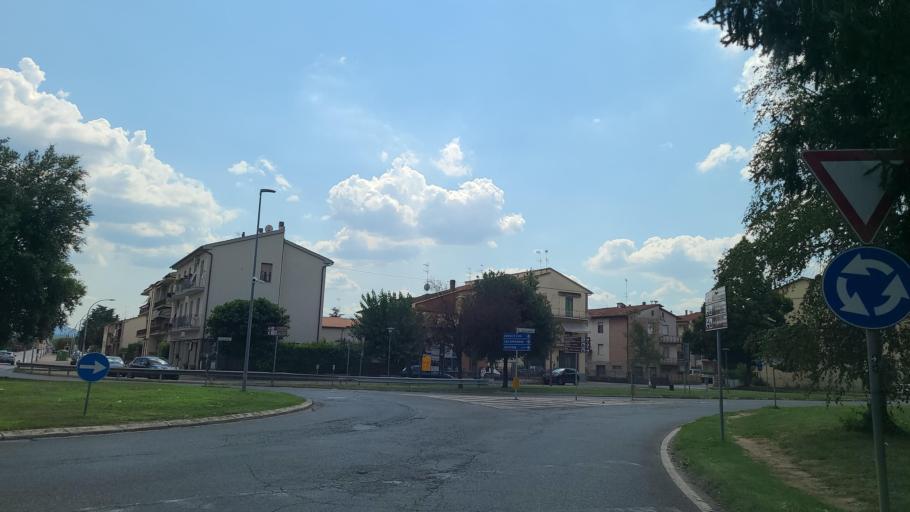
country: IT
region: Tuscany
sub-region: Provincia di Siena
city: Colle di Val d'Elsa
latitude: 43.4160
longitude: 11.1317
